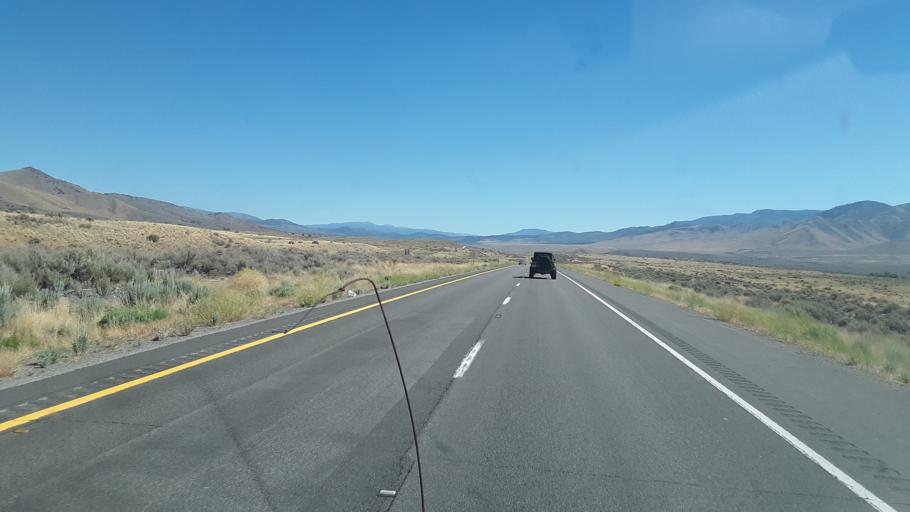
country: US
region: Nevada
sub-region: Washoe County
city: Cold Springs
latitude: 39.7602
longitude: -120.0392
